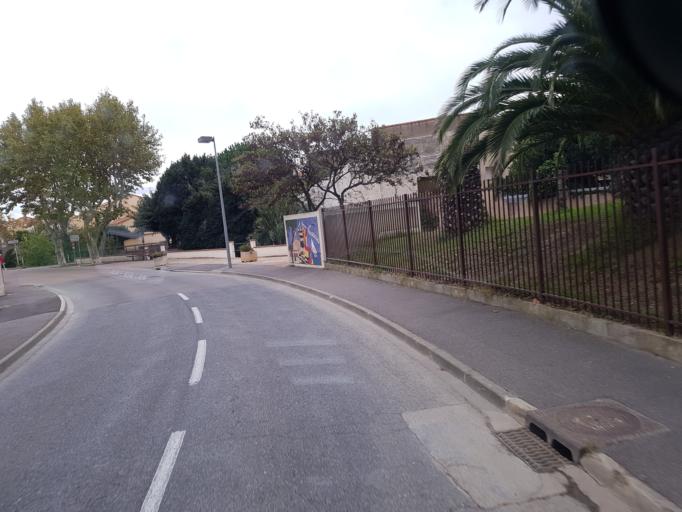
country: FR
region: Languedoc-Roussillon
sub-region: Departement des Pyrenees-Orientales
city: Torreilles
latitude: 42.7551
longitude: 2.9958
